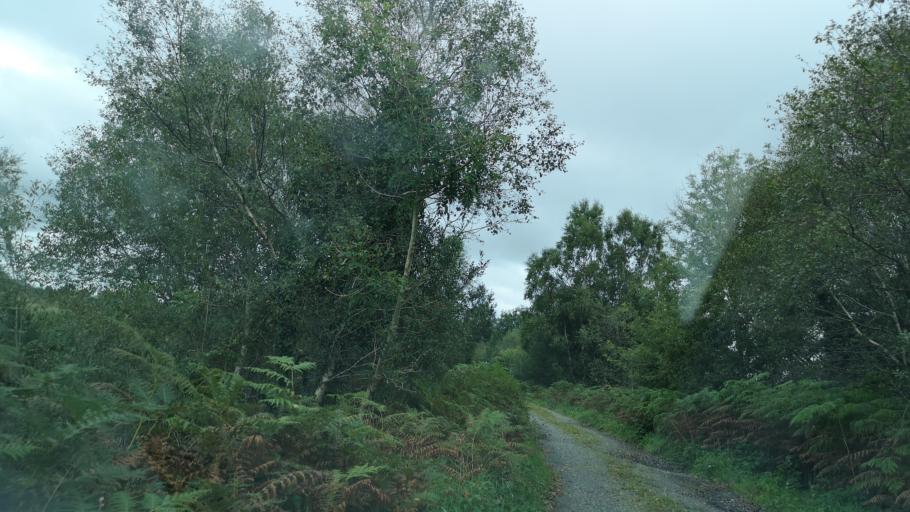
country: IE
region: Connaught
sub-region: County Galway
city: Athenry
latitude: 53.3020
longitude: -8.6512
